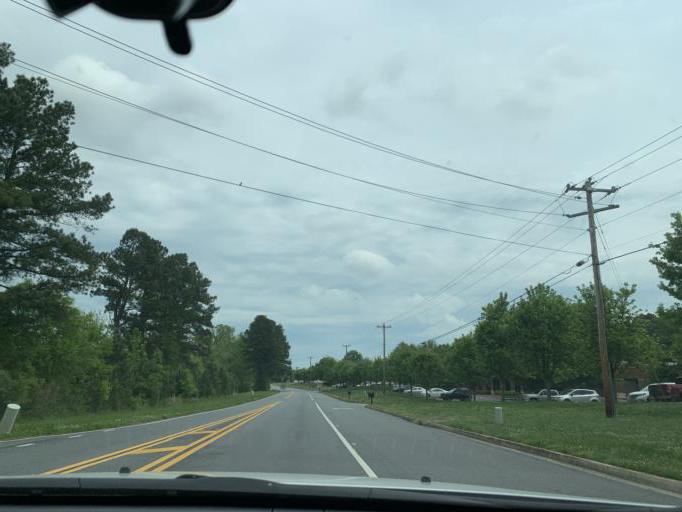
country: US
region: Georgia
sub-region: Fulton County
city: Milton
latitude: 34.1326
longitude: -84.2101
